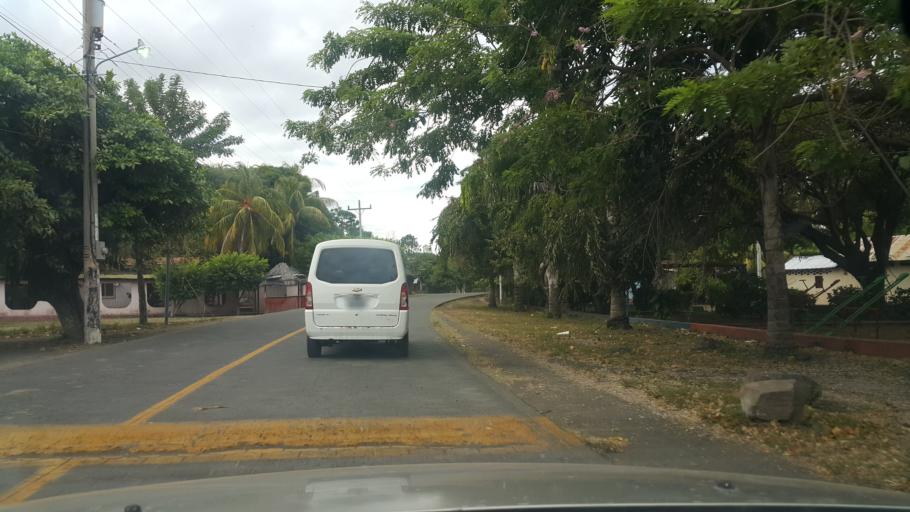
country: NI
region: Rivas
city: Moyogalpa
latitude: 11.4966
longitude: -85.6950
